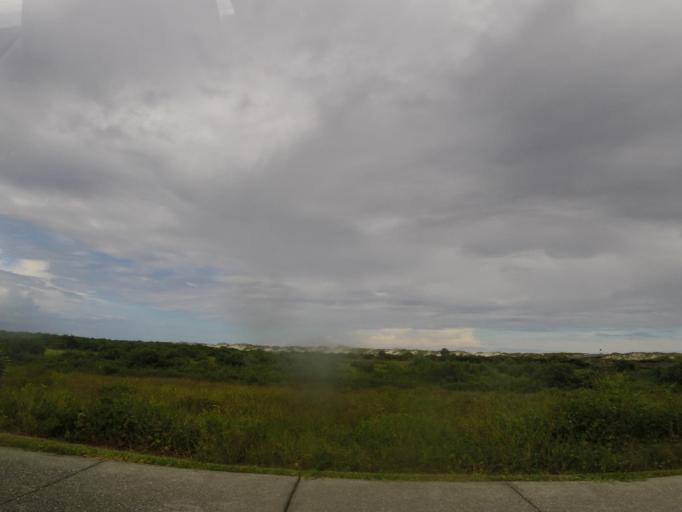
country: US
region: Florida
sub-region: Saint Johns County
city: Saint Augustine Beach
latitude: 29.8663
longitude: -81.2710
